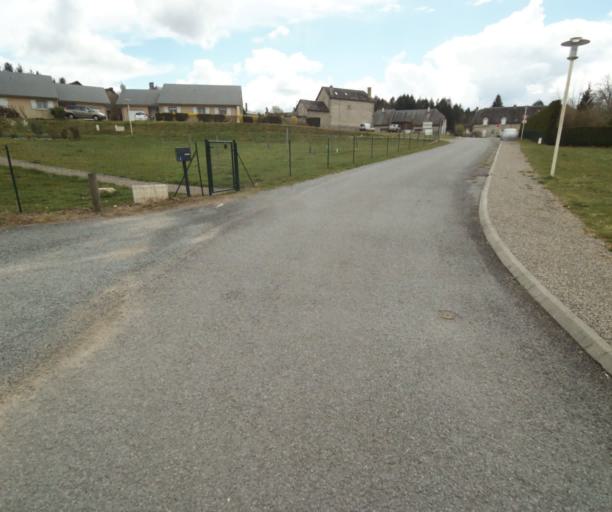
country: FR
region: Limousin
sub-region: Departement de la Correze
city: Correze
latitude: 45.3360
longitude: 1.9448
